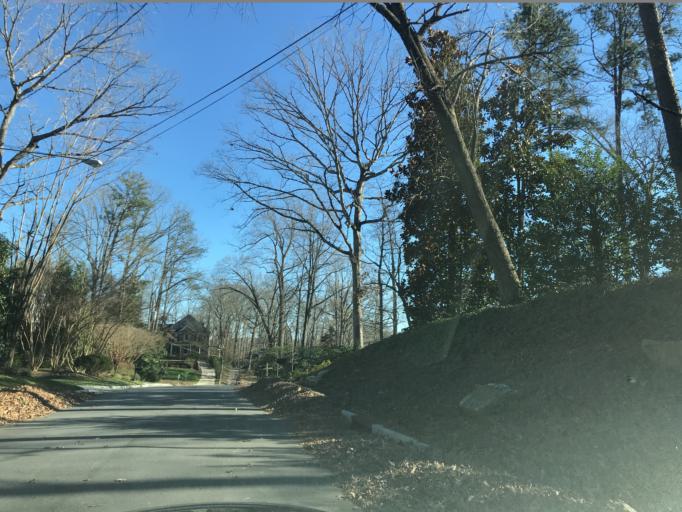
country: US
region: North Carolina
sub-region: Wake County
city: West Raleigh
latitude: 35.8262
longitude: -78.6544
